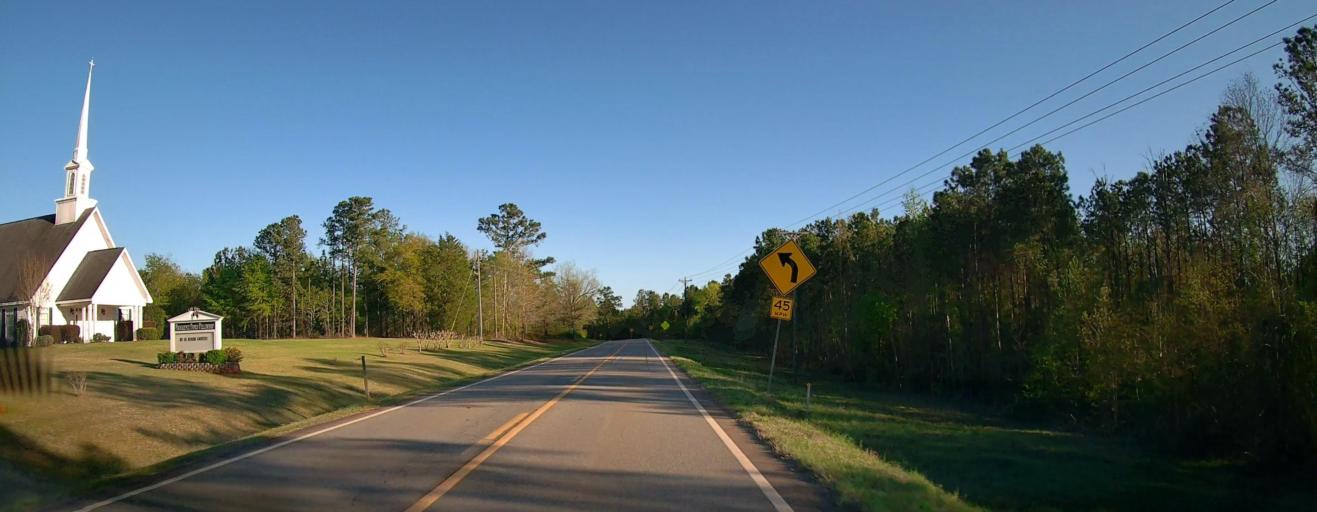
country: US
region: Georgia
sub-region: Wilkinson County
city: Irwinton
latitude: 32.8691
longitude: -83.0946
